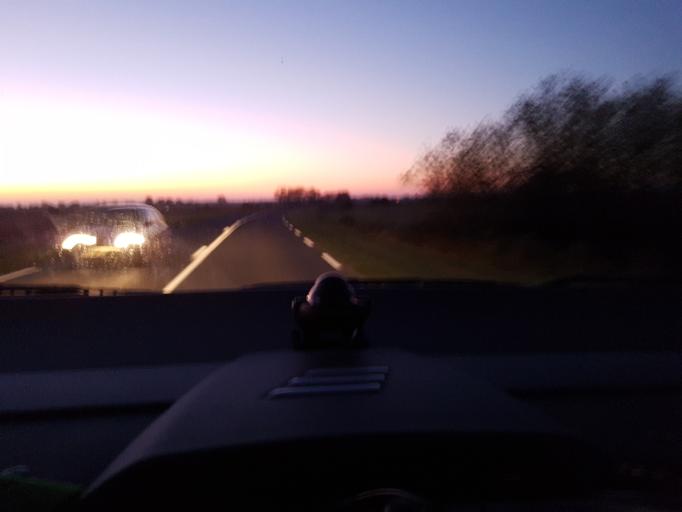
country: FR
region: Picardie
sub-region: Departement de la Somme
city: Pende
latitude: 50.1851
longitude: 1.5823
